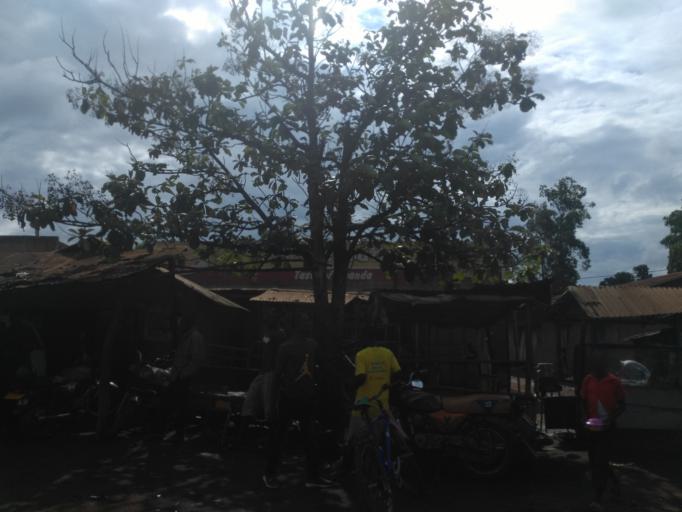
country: UG
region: Central Region
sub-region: Buikwe District
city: Njeru
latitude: 0.3966
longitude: 33.1741
